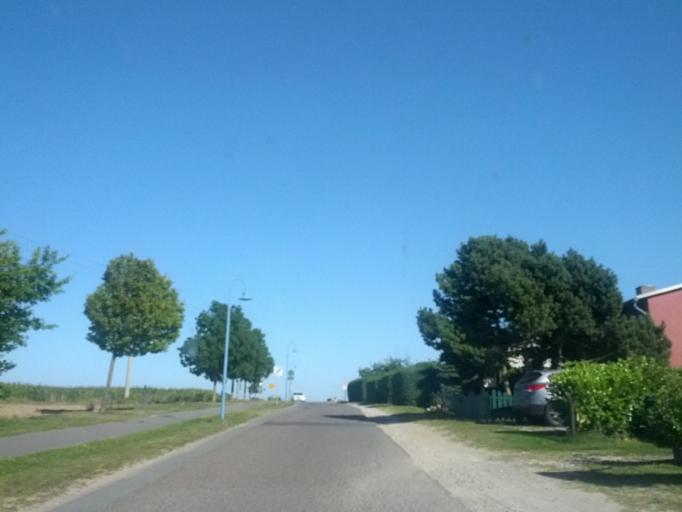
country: DE
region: Mecklenburg-Vorpommern
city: Ostseebad Gohren
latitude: 54.3303
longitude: 13.6928
